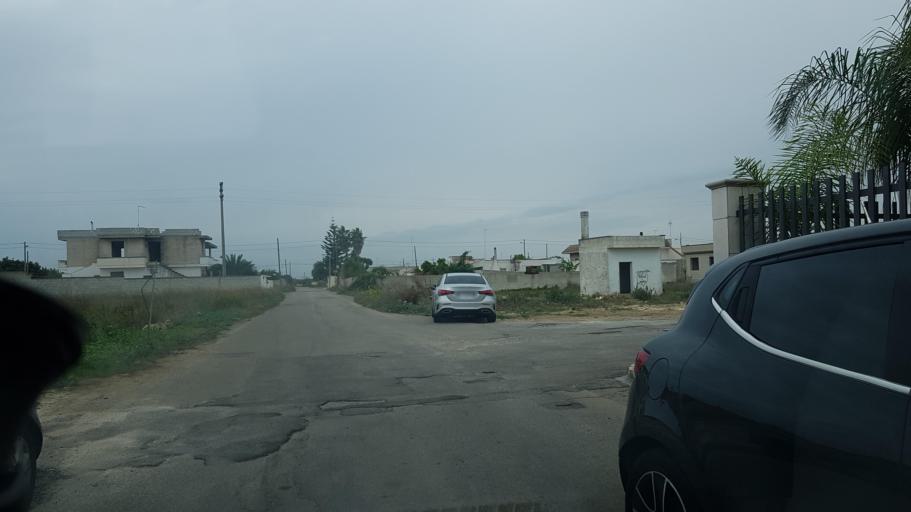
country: IT
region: Apulia
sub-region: Provincia di Brindisi
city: Cellino San Marco
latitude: 40.4743
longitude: 17.9592
